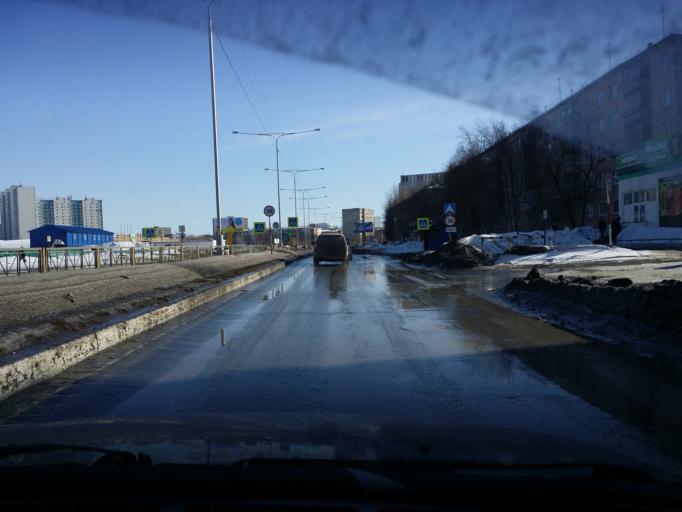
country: RU
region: Khanty-Mansiyskiy Avtonomnyy Okrug
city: Nizhnevartovsk
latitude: 60.9489
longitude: 76.5638
